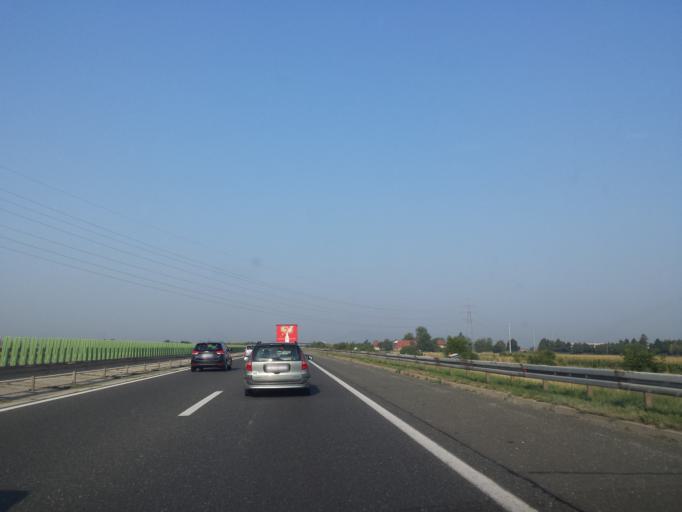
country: HR
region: Grad Zagreb
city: Zadvorsko
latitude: 45.7500
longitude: 15.9451
